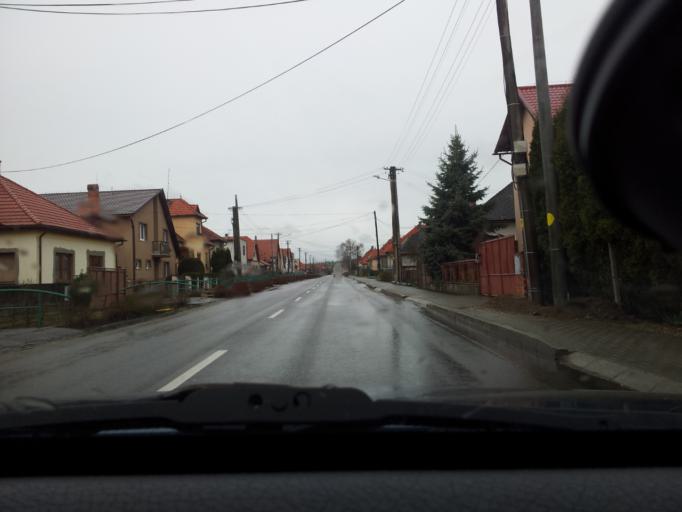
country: SK
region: Nitriansky
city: Tlmace
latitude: 48.3139
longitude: 18.5304
